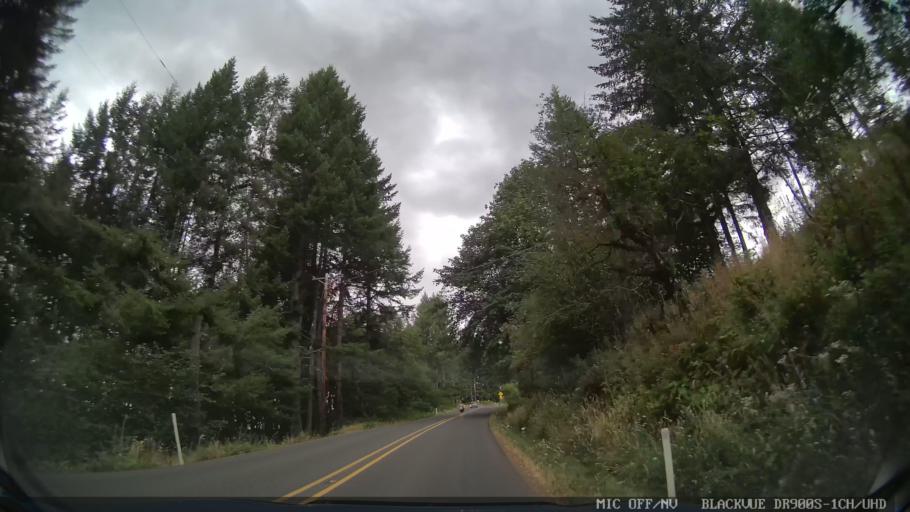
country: US
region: Oregon
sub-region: Linn County
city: Lyons
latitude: 44.8511
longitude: -122.6641
